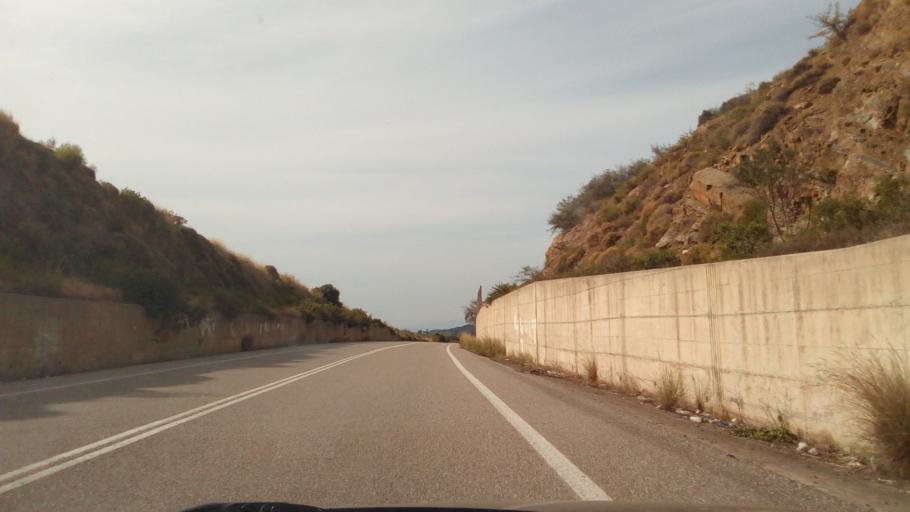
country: GR
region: West Greece
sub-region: Nomos Aitolias kai Akarnanias
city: Nafpaktos
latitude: 38.3820
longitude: 21.7918
